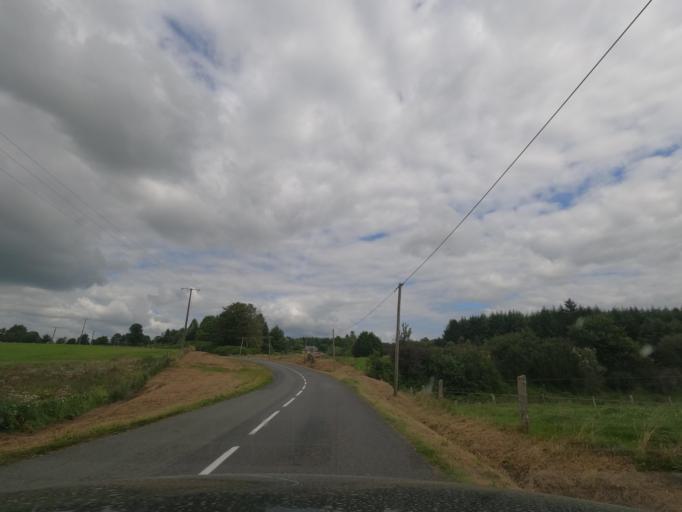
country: FR
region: Lower Normandy
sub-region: Departement de la Manche
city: Le Teilleul
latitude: 48.5032
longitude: -0.9131
